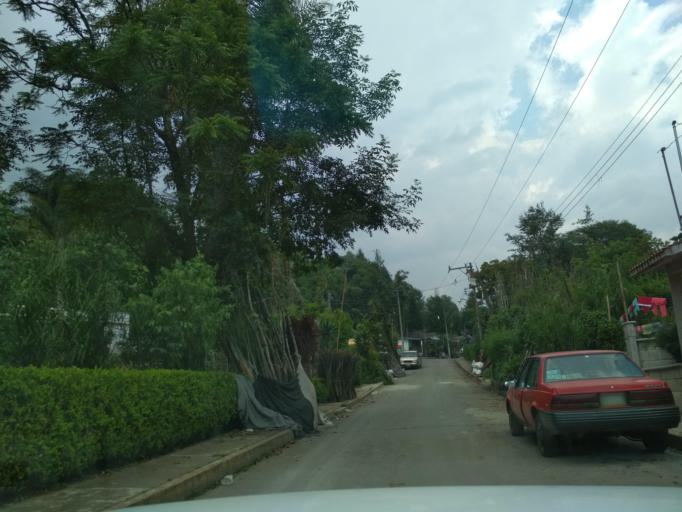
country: MX
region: Veracruz
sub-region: Mariano Escobedo
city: Mariano Escobedo
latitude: 18.9152
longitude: -97.1333
